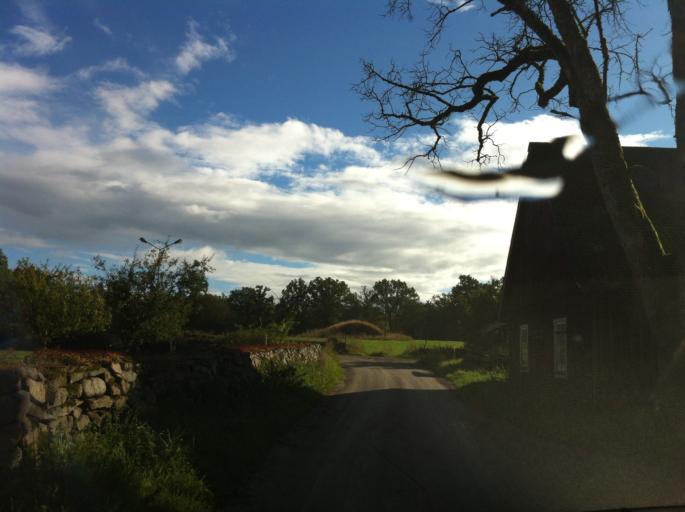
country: SE
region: Skane
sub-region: Hassleholms Kommun
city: Sosdala
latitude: 56.1230
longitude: 13.5970
